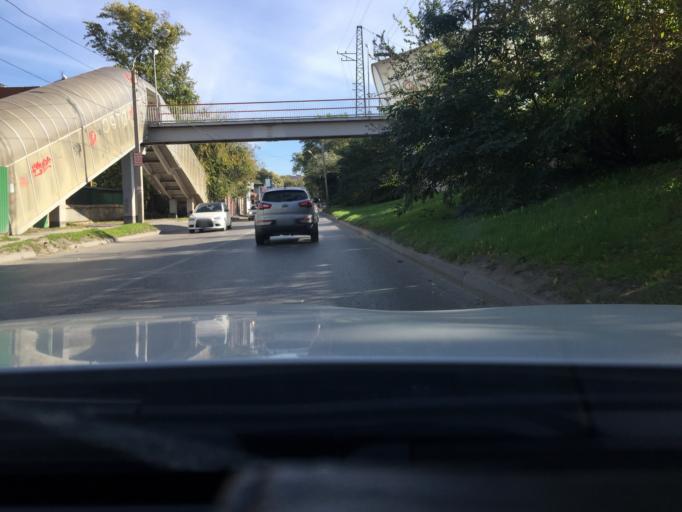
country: RU
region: Rostov
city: Rostov-na-Donu
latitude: 47.2455
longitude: 39.7494
